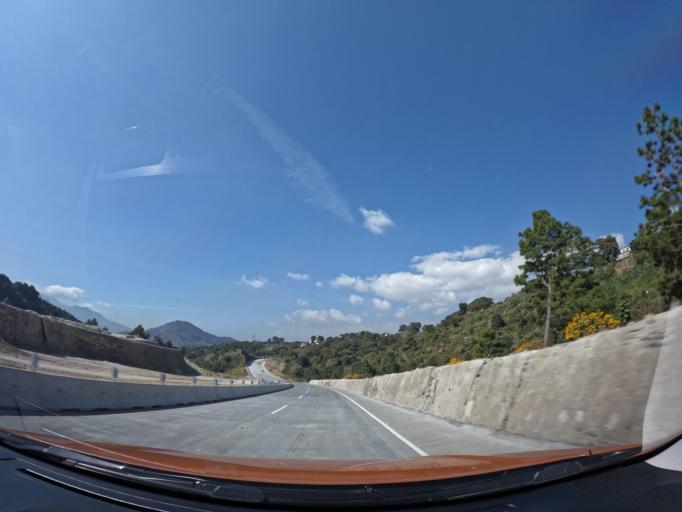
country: GT
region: Guatemala
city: Villa Canales
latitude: 14.4939
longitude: -90.5221
